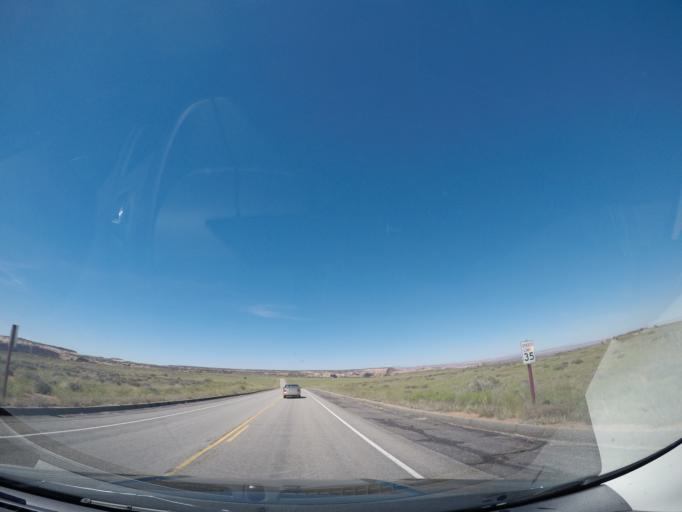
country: US
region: Utah
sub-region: Grand County
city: Moab
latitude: 38.4708
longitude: -109.8127
